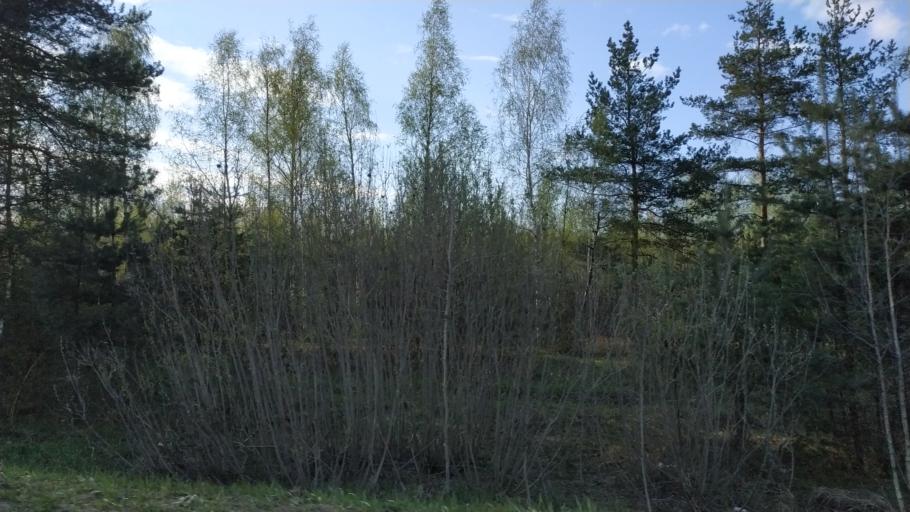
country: RU
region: Moskovskaya
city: Fryazevo
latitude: 55.7406
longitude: 38.5235
